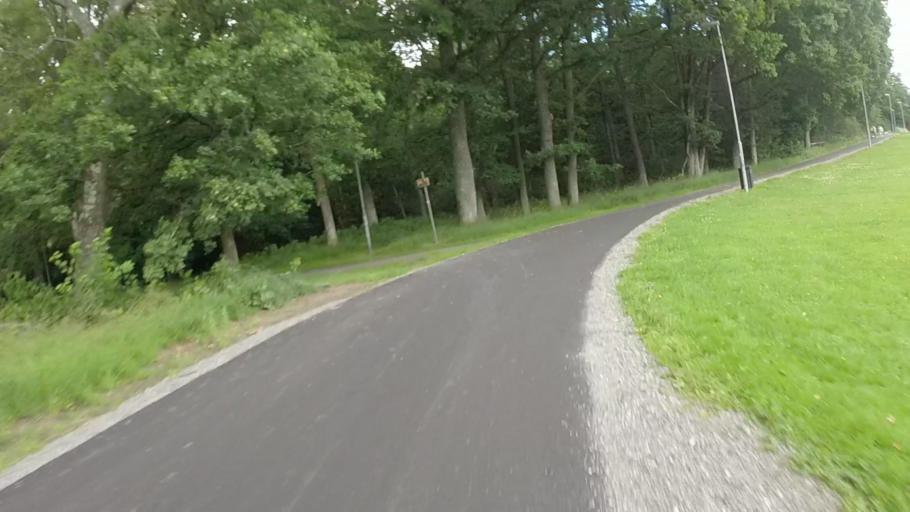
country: SE
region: Vaestra Goetaland
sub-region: Trollhattan
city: Trollhattan
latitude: 58.2719
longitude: 12.3062
